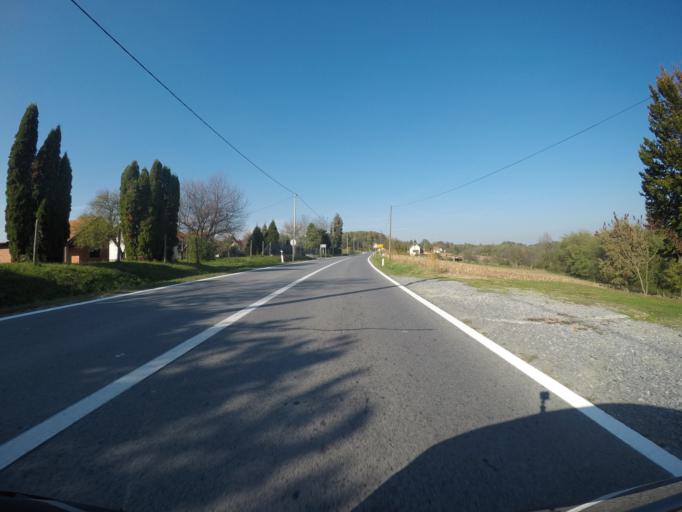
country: HR
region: Bjelovarsko-Bilogorska
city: Bjelovar
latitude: 45.9797
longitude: 16.8946
